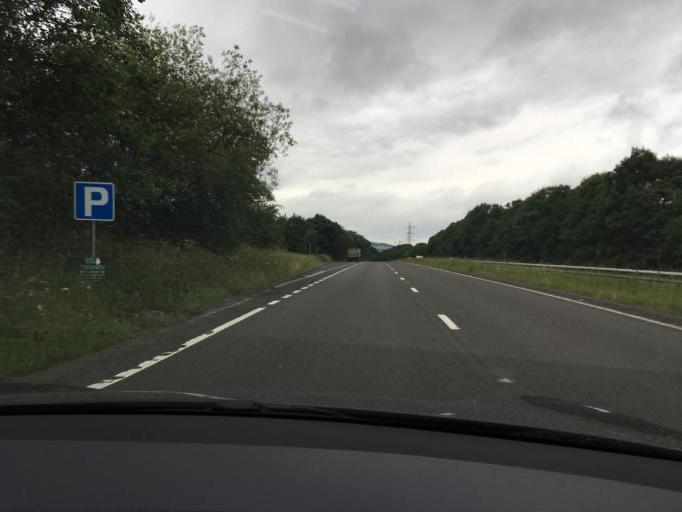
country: GB
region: England
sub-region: Derbyshire
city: Chinley
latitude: 53.3328
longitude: -1.9319
